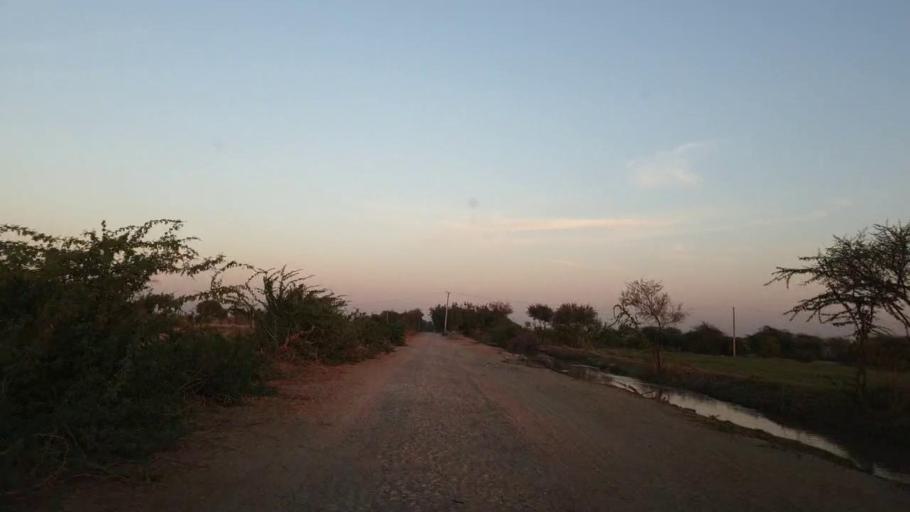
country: PK
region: Sindh
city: Kunri
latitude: 25.1468
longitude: 69.4433
